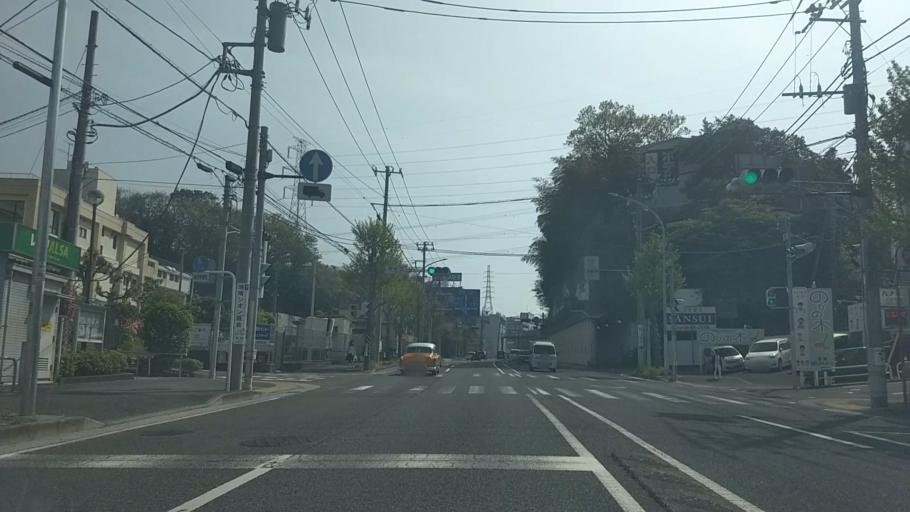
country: JP
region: Kanagawa
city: Kamakura
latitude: 35.3791
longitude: 139.5702
